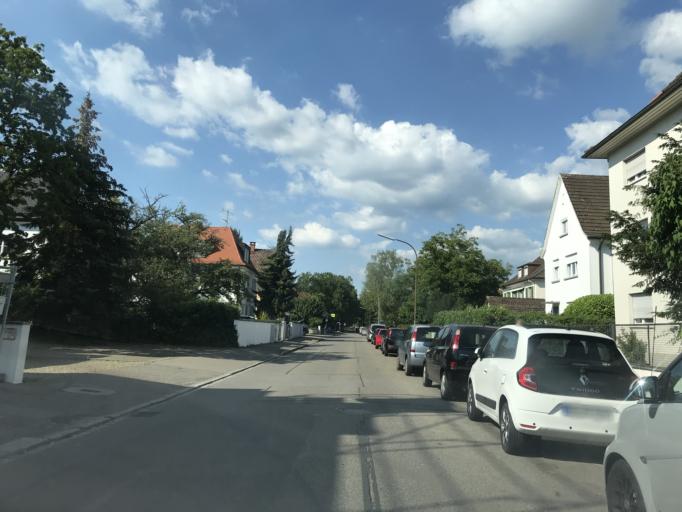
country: DE
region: Baden-Wuerttemberg
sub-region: Freiburg Region
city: Loerrach
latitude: 47.6189
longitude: 7.6643
